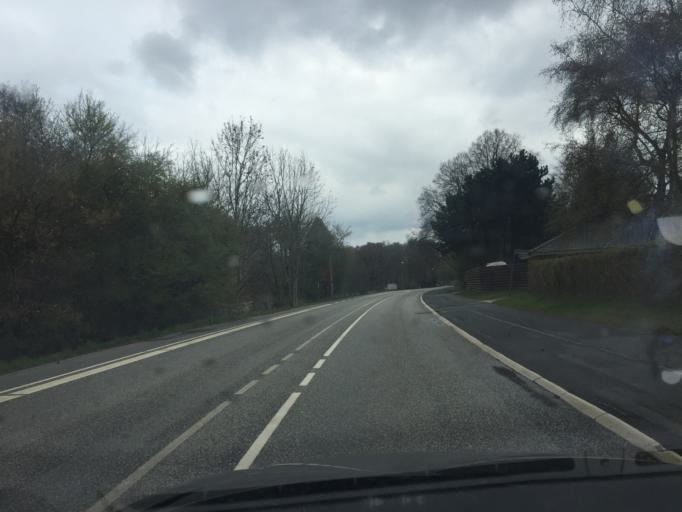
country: DK
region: Capital Region
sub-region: Halsnaes Kommune
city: Frederiksvaerk
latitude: 55.9960
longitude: 12.0138
